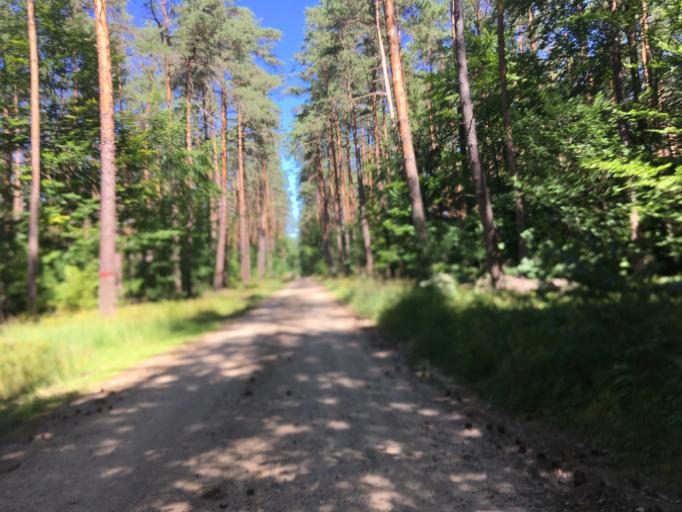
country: DE
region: Brandenburg
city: Rheinsberg
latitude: 53.1193
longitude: 12.9646
